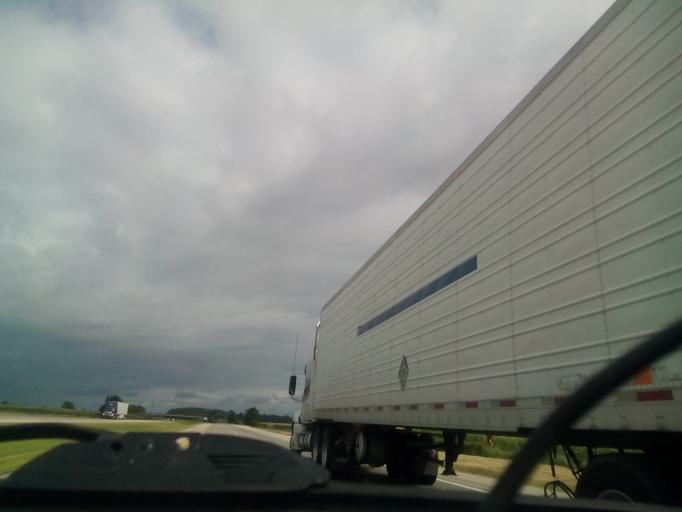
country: US
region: Ohio
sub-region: Williams County
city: Montpelier
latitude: 41.6166
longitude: -84.6427
